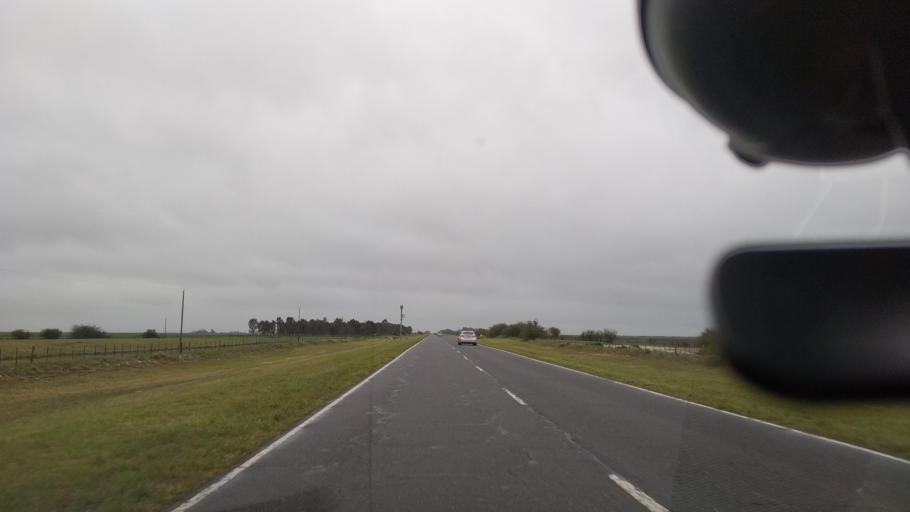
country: AR
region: Buenos Aires
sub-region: Partido de Dolores
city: Dolores
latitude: -36.0770
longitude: -57.4387
